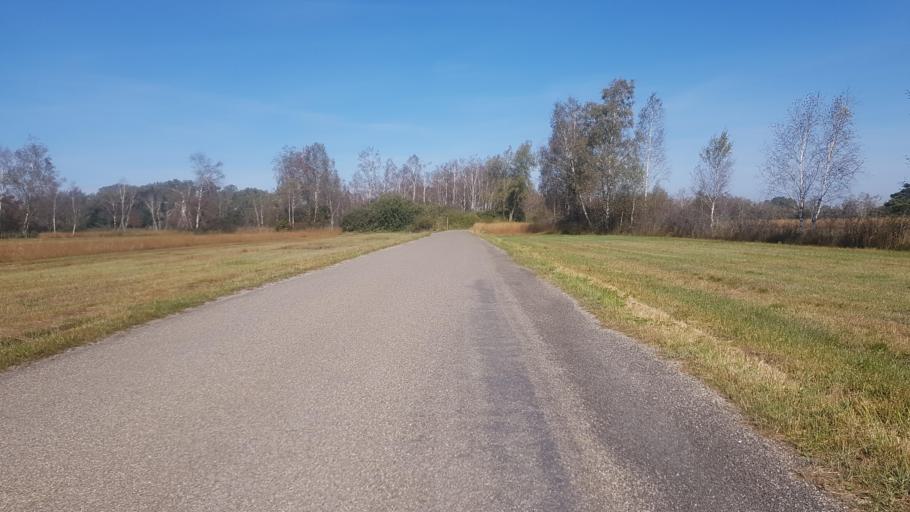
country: AT
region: Vorarlberg
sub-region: Politischer Bezirk Bregenz
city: Hochst
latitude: 47.4901
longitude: 9.6256
